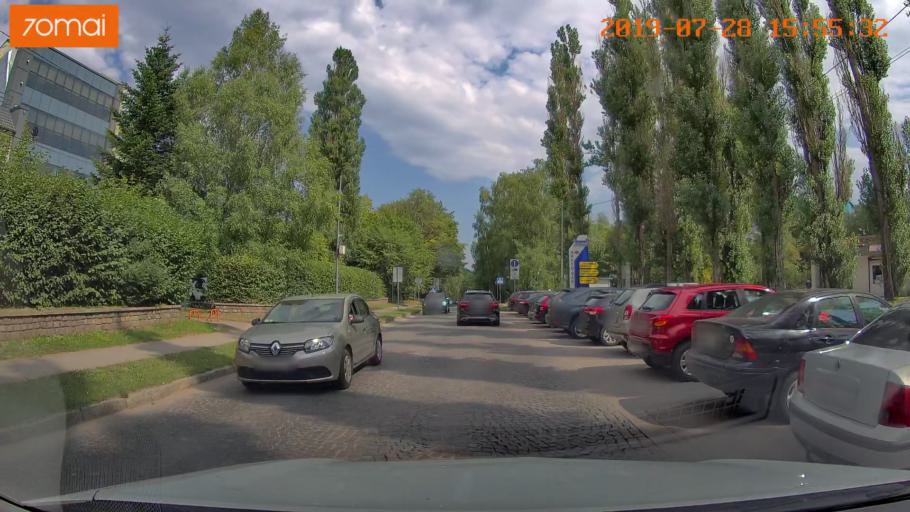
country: RU
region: Kaliningrad
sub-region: Gorod Svetlogorsk
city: Svetlogorsk
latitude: 54.9409
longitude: 20.1404
